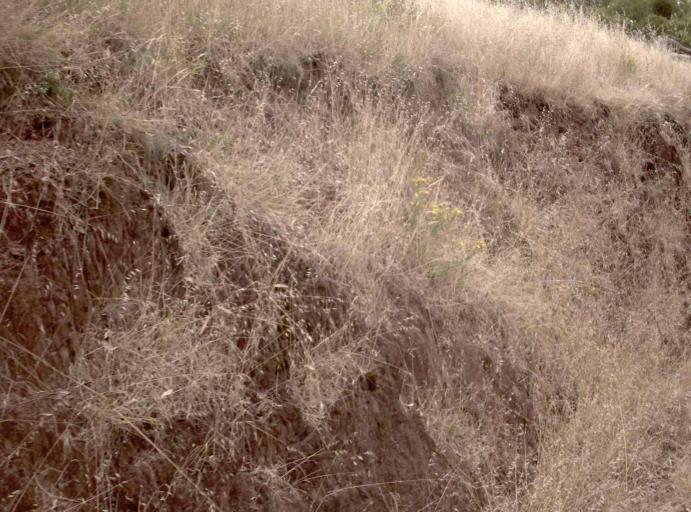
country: AU
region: Victoria
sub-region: Wellington
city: Heyfield
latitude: -37.6892
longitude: 146.6544
